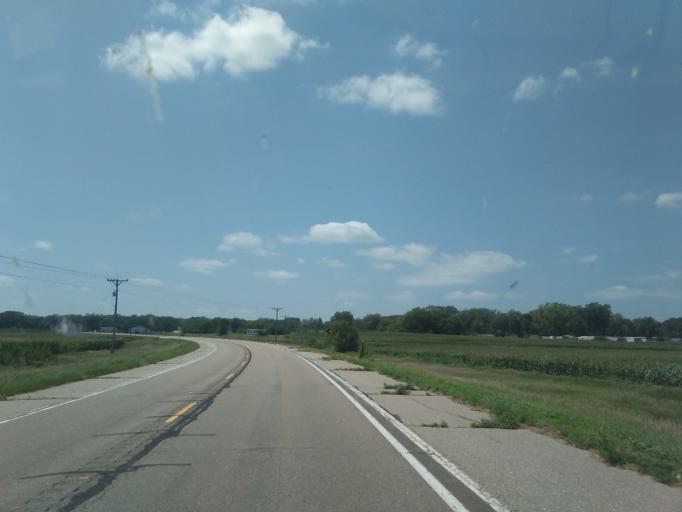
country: US
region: Nebraska
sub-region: Gosper County
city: Elwood
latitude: 40.6847
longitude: -99.8211
